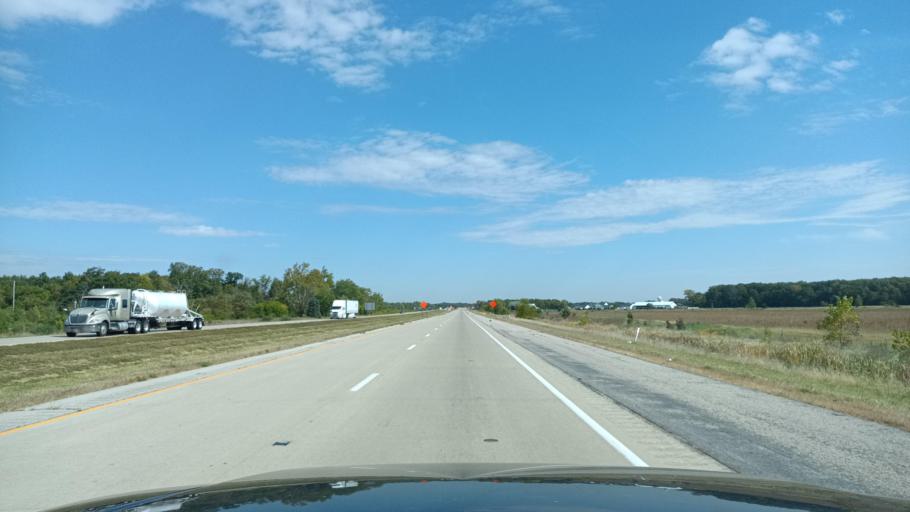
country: US
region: Indiana
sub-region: Allen County
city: New Haven
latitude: 41.0930
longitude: -84.9783
